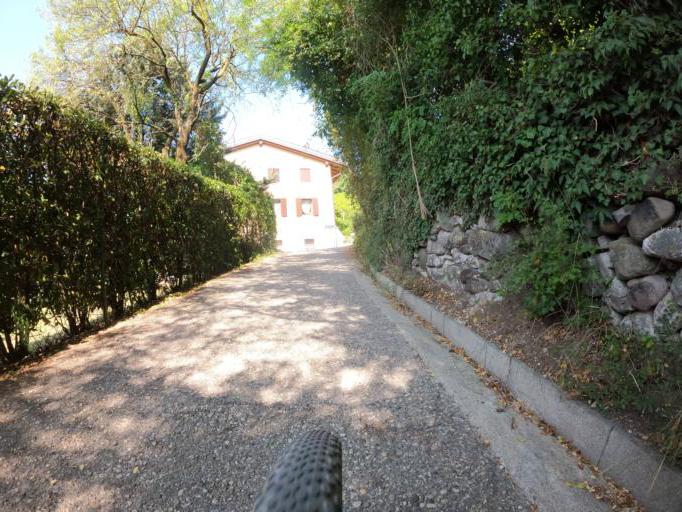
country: IT
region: Veneto
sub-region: Provincia di Verona
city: Costermano
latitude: 45.5797
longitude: 10.7430
